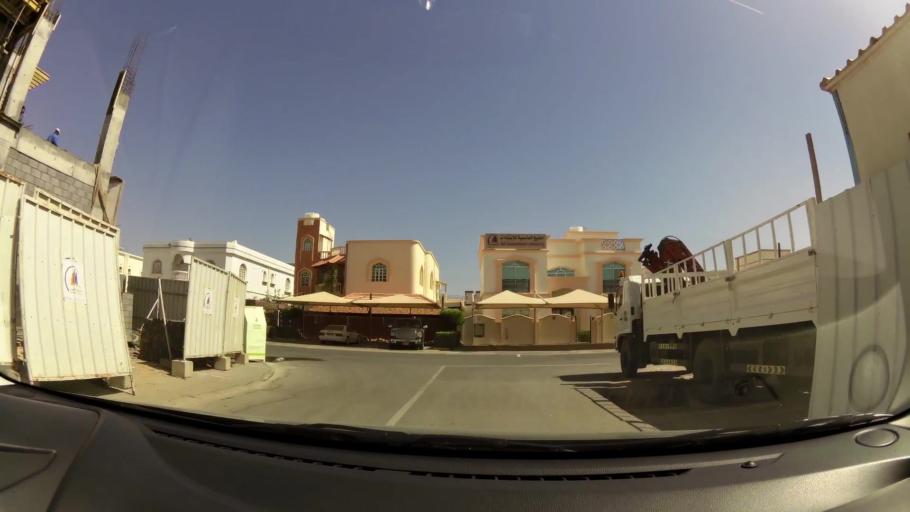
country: OM
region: Muhafazat Masqat
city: As Sib al Jadidah
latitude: 23.5957
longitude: 58.2473
